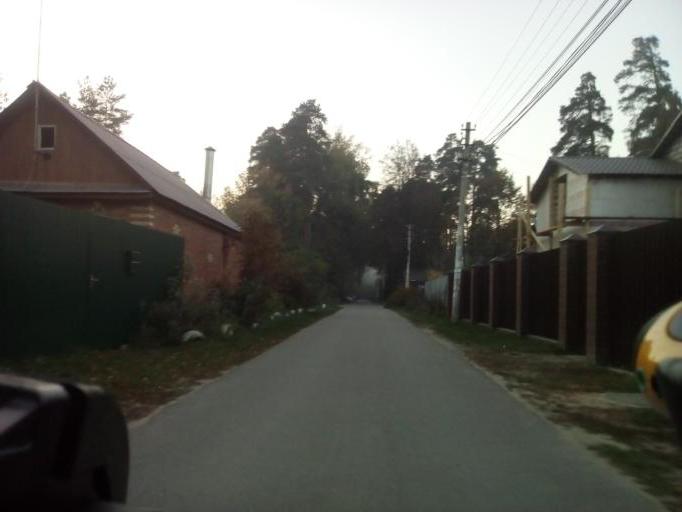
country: RU
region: Moskovskaya
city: Kratovo
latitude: 55.6026
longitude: 38.1790
